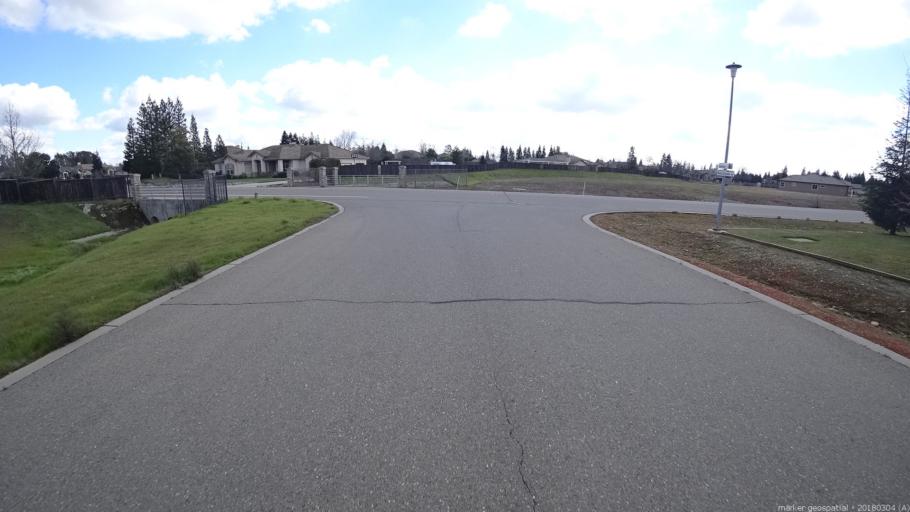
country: US
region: California
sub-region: Sacramento County
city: Vineyard
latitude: 38.4633
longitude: -121.3014
